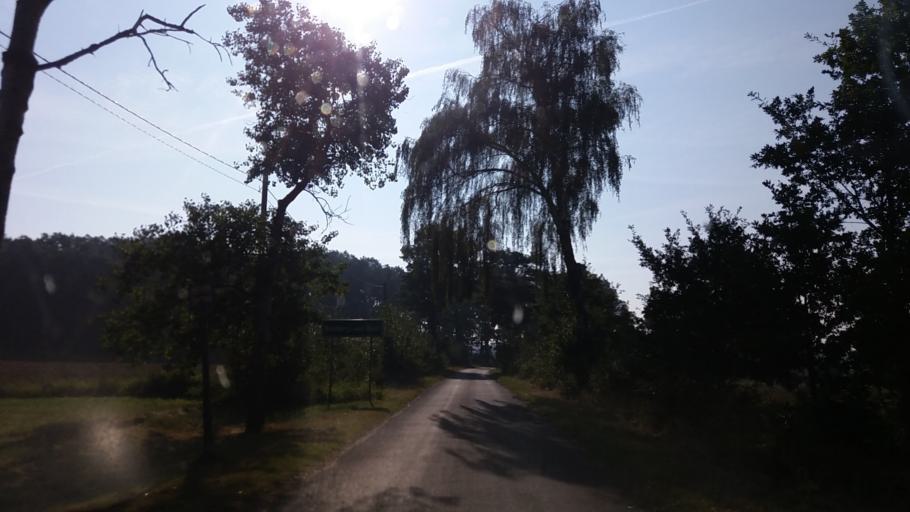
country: PL
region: West Pomeranian Voivodeship
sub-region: Powiat choszczenski
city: Pelczyce
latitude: 52.9996
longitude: 15.3652
